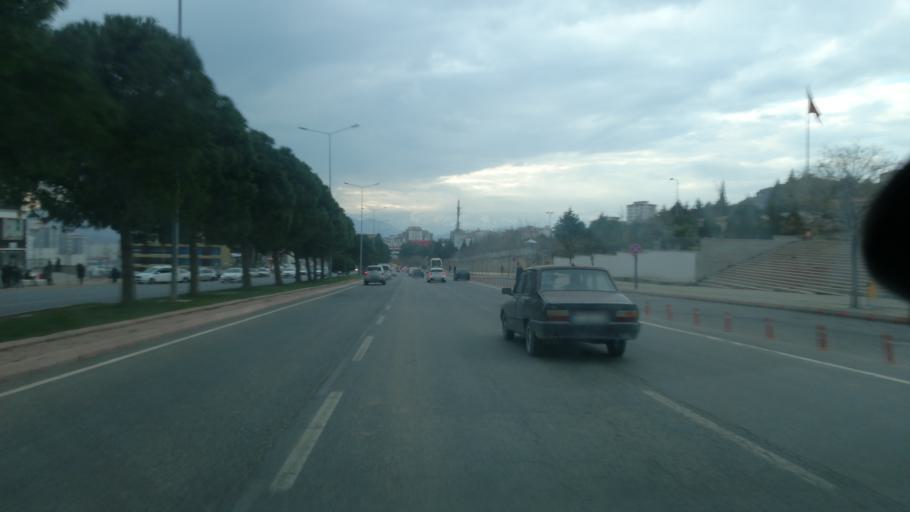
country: TR
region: Kahramanmaras
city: Kahramanmaras
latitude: 37.5996
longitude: 36.8372
